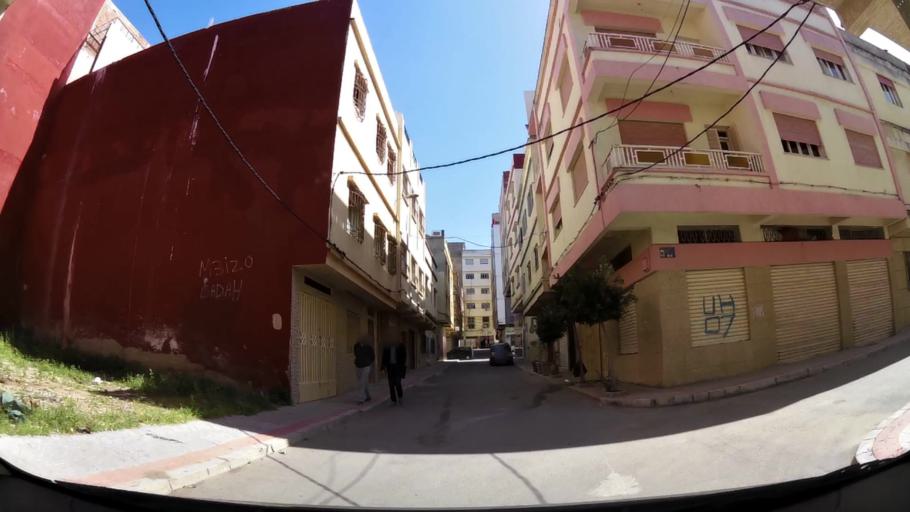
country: MA
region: Tanger-Tetouan
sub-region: Tanger-Assilah
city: Tangier
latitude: 35.7486
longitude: -5.8115
